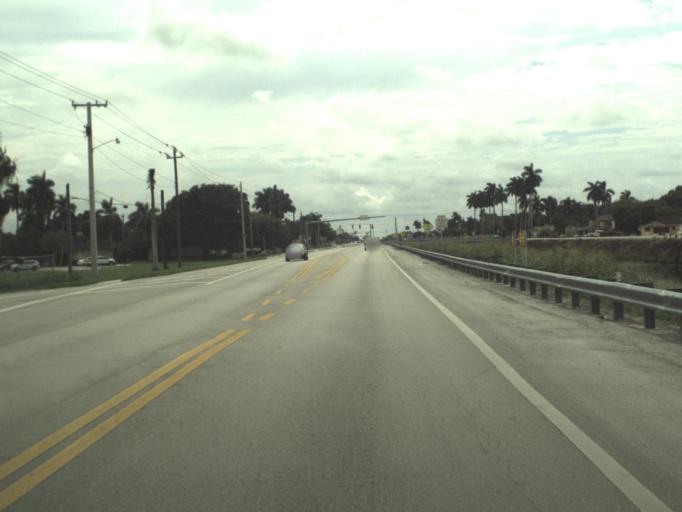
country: US
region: Florida
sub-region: Palm Beach County
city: Belle Glade
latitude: 26.6913
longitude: -80.6780
